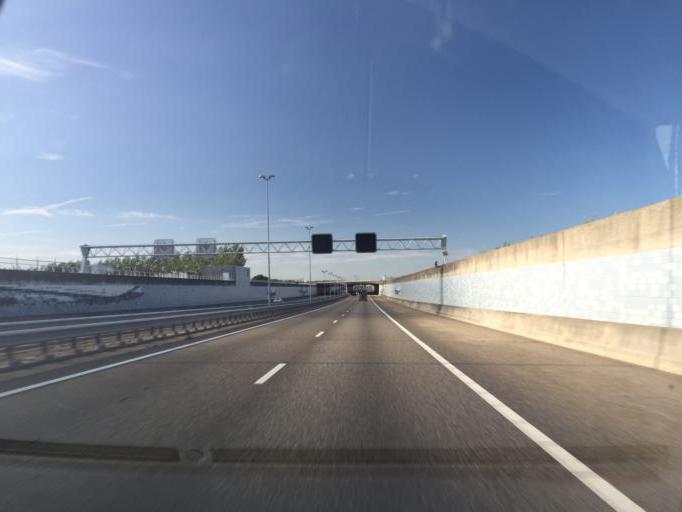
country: NL
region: North Holland
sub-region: Gemeente Haarlemmermeer
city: Hoofddorp
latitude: 52.3179
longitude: 4.7331
